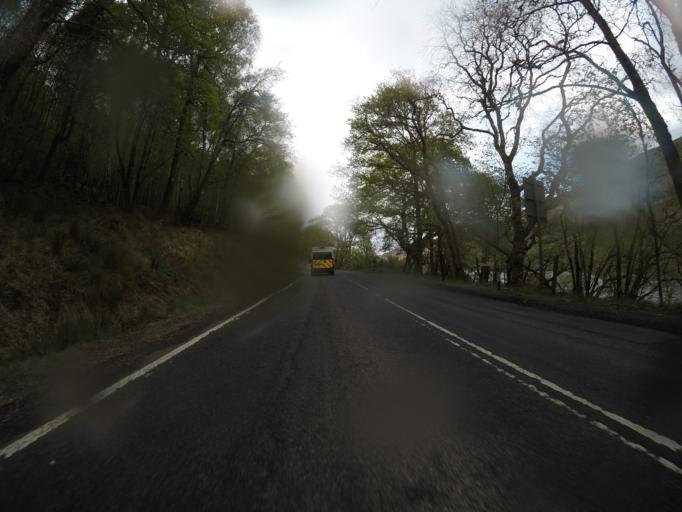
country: GB
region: Scotland
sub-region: Highland
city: Spean Bridge
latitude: 57.0564
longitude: -4.7900
